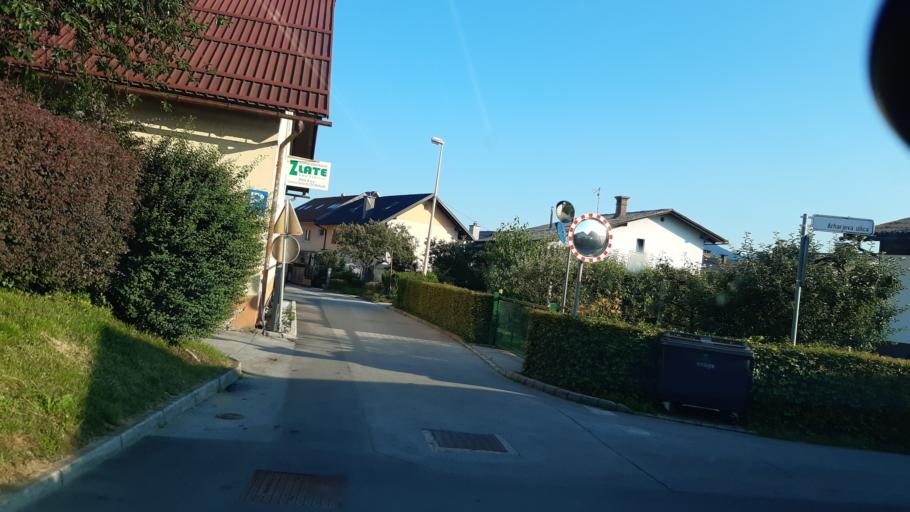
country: SI
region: Medvode
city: Medvode
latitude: 46.1447
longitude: 14.4036
